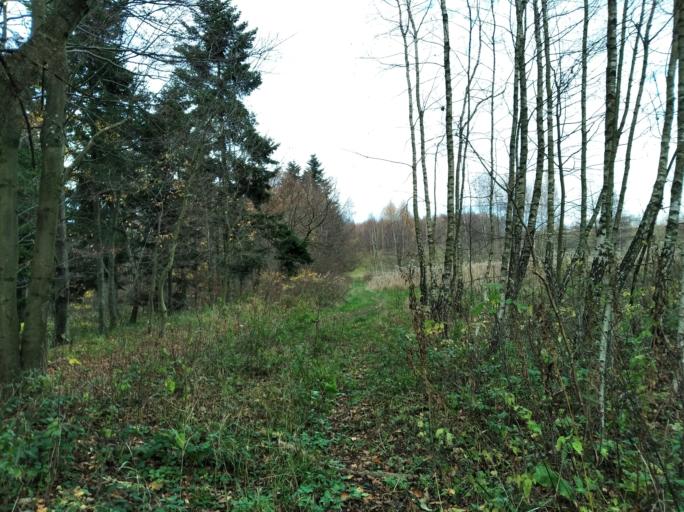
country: PL
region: Subcarpathian Voivodeship
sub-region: Powiat strzyzowski
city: Jawornik
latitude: 49.8659
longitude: 21.8561
